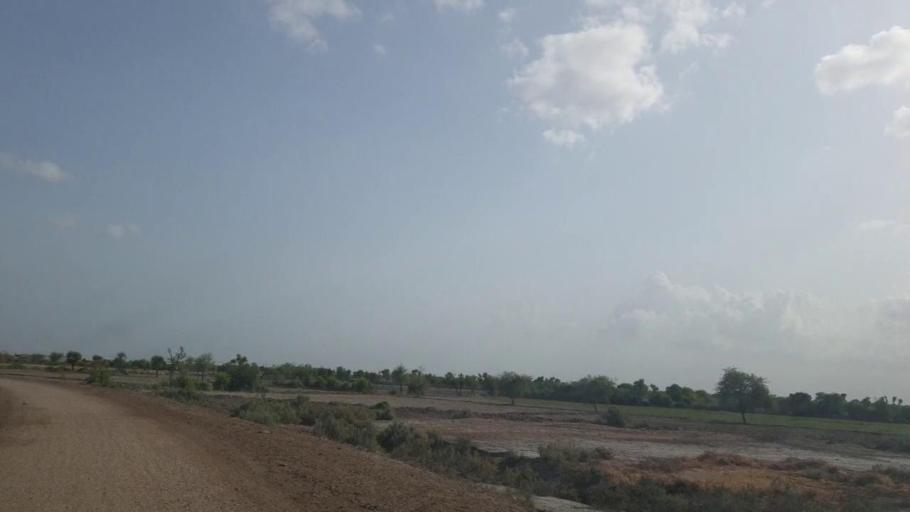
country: PK
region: Sindh
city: Tando Bago
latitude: 24.8261
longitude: 69.1208
